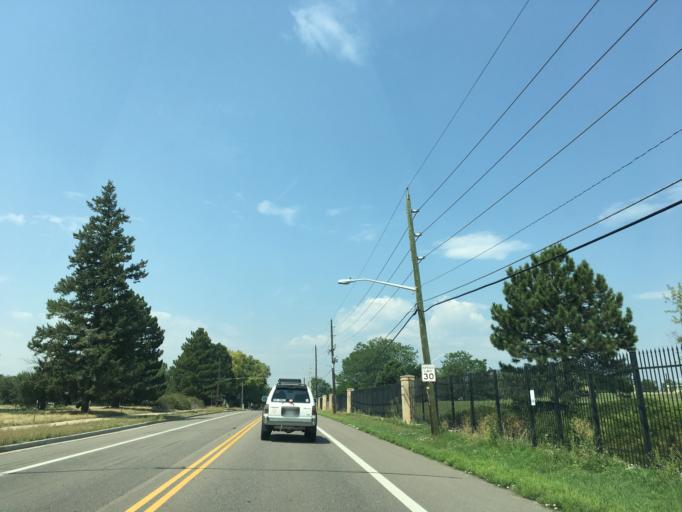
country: US
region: Colorado
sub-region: Jefferson County
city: Applewood
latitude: 39.7475
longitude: -105.1219
